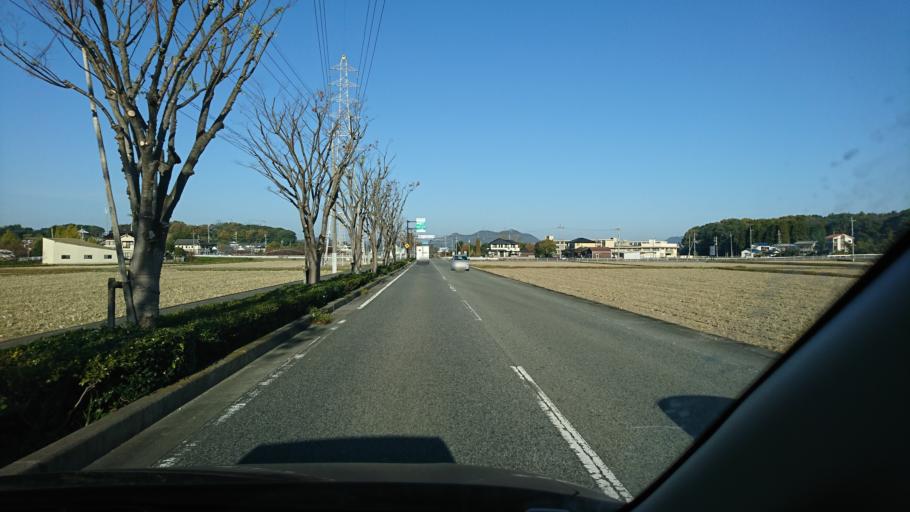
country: JP
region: Hyogo
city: Kakogawacho-honmachi
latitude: 34.7725
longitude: 134.8799
